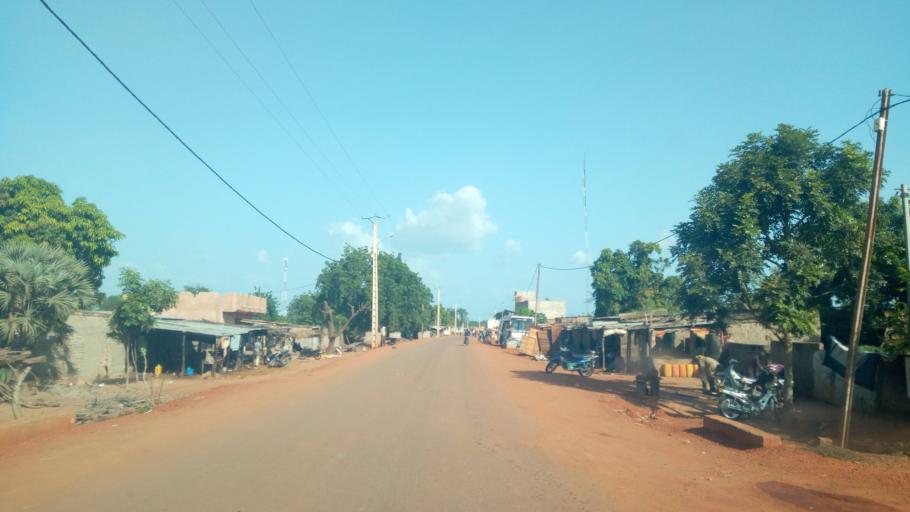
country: ML
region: Sikasso
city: Yorosso
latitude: 12.1837
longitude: -4.8069
